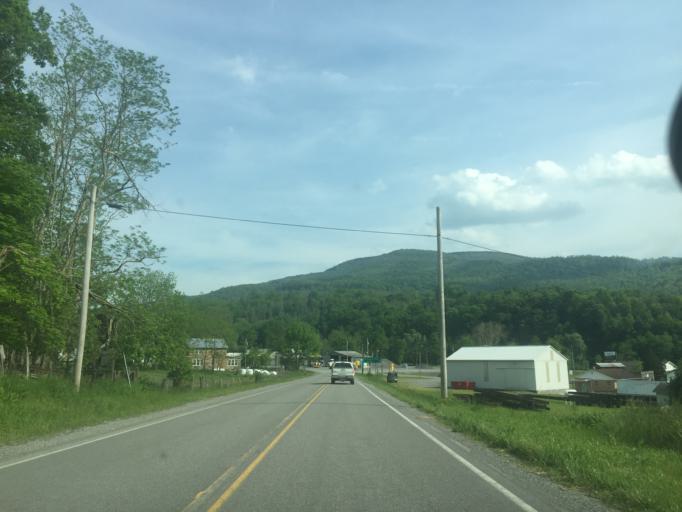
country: US
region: West Virginia
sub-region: Tucker County
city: Parsons
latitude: 38.9236
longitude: -79.5240
